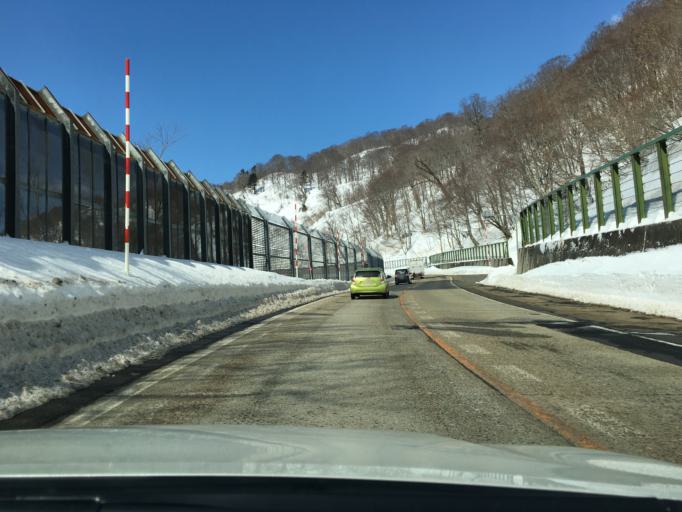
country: JP
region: Yamagata
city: Tsuruoka
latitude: 38.4893
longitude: 139.9845
